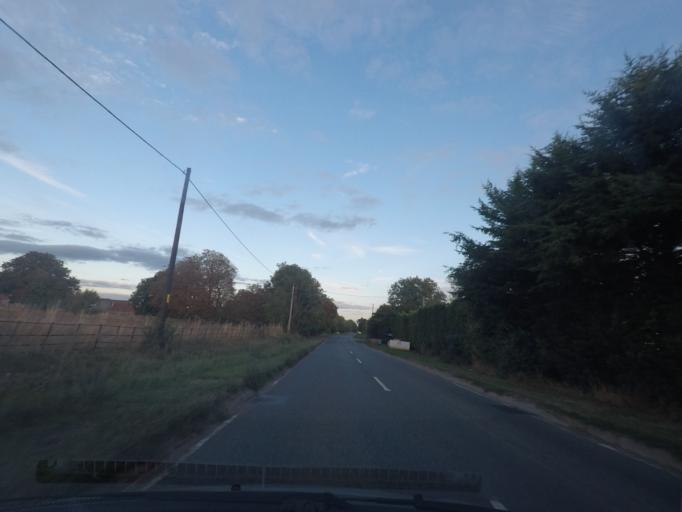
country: GB
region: England
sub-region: Oxfordshire
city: Faringdon
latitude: 51.6538
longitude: -1.5638
